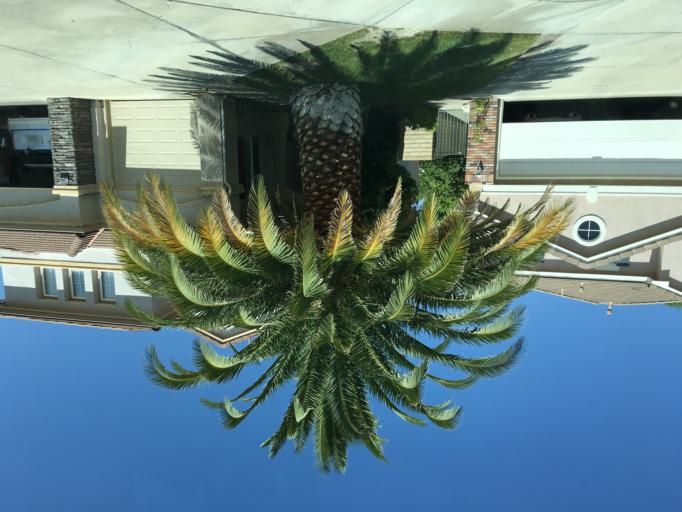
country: US
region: California
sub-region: Los Angeles County
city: Santa Clarita
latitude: 34.3854
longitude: -118.5966
